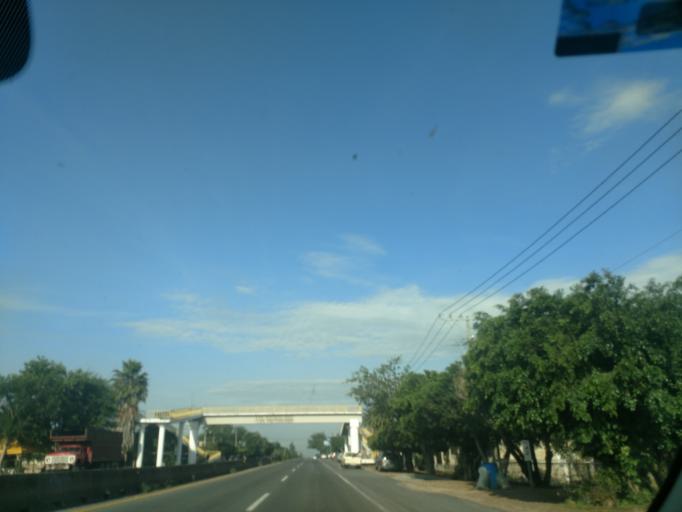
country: MX
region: Jalisco
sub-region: Ameca
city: Los Pocitos
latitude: 20.5370
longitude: -103.9370
